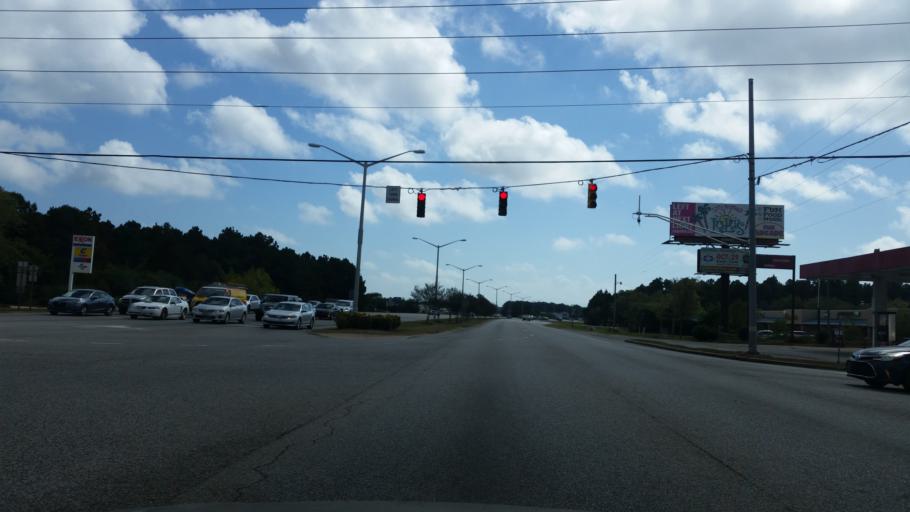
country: US
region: Alabama
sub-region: Baldwin County
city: Gulf Shores
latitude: 30.2975
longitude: -87.6832
